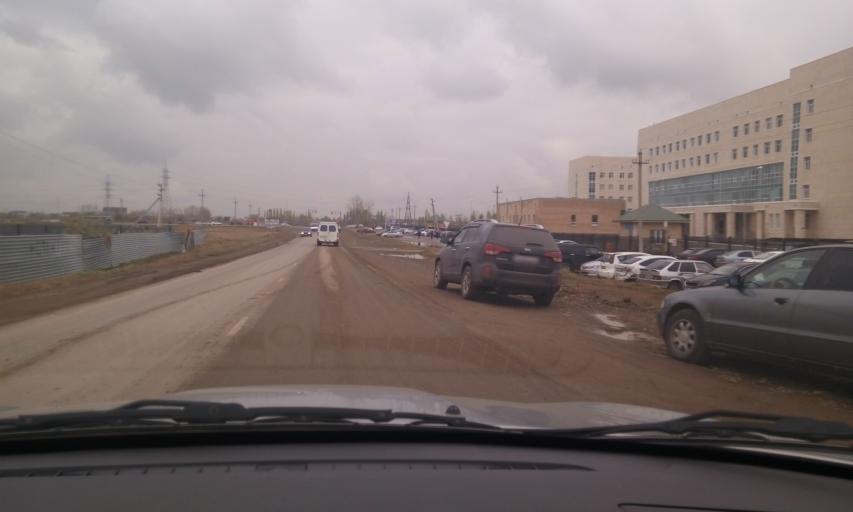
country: KZ
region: Astana Qalasy
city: Astana
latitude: 51.1410
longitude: 71.5309
